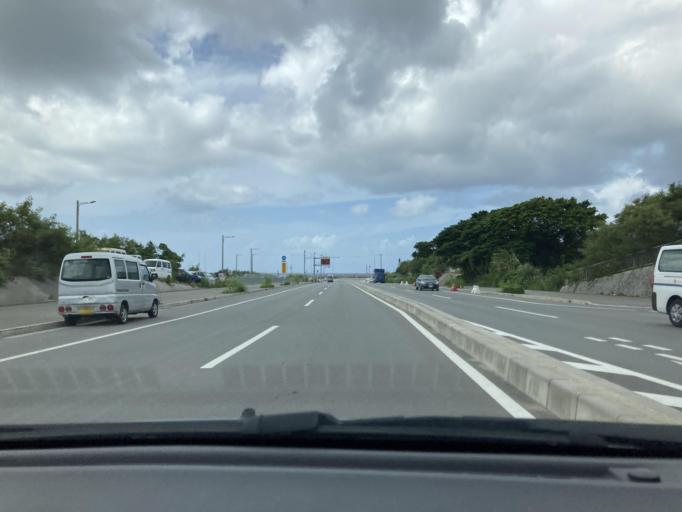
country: JP
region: Okinawa
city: Ginowan
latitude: 26.2700
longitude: 127.7086
